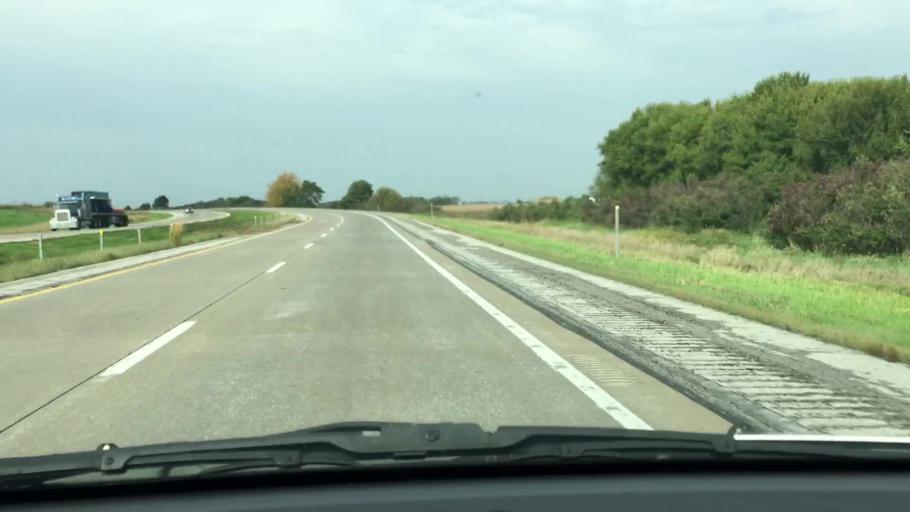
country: US
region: Iowa
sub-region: Scott County
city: Walcott
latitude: 41.6322
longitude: -90.8349
